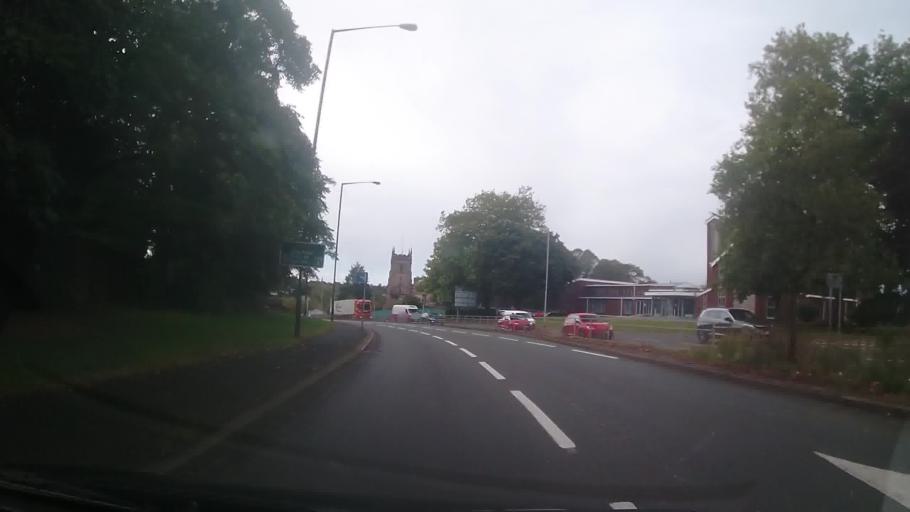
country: GB
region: England
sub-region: Worcestershire
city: Kidderminster
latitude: 52.3909
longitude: -2.2482
